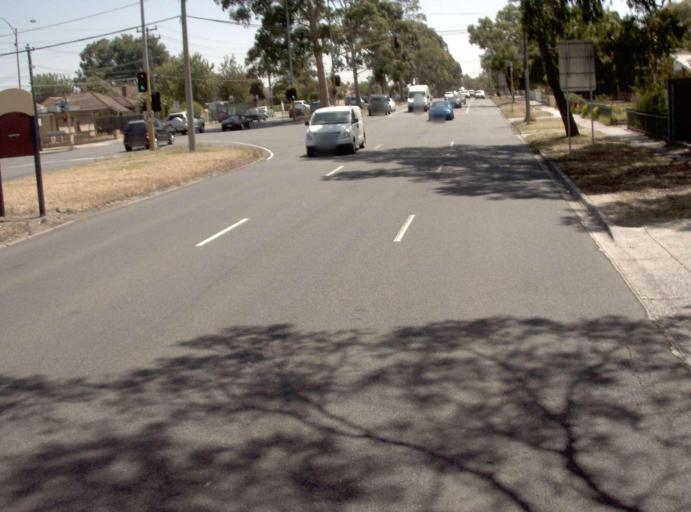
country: AU
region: Victoria
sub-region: Banyule
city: Bellfield
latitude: -37.7496
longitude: 145.0407
